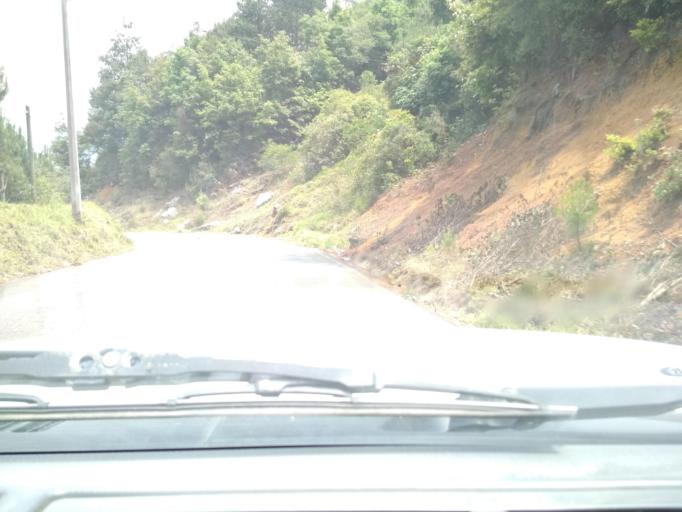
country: MX
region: Veracruz
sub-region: Camerino Z. Mendoza
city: Necoxtla
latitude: 18.7855
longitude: -97.1551
